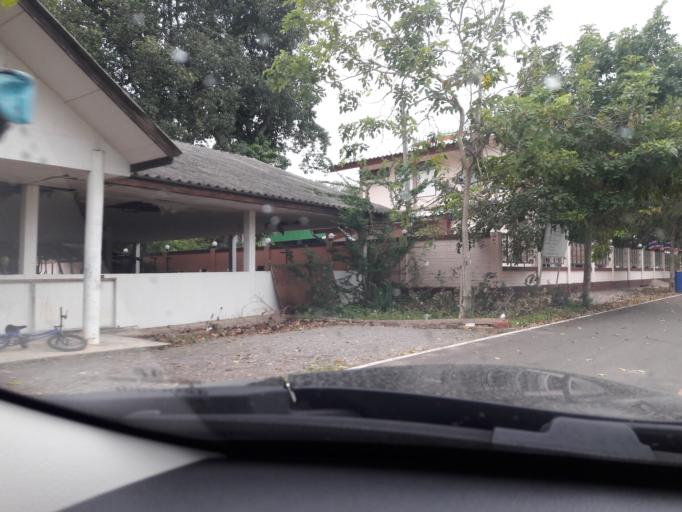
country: TH
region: Ratchaburi
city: Bang Phae
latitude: 13.5995
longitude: 99.9015
